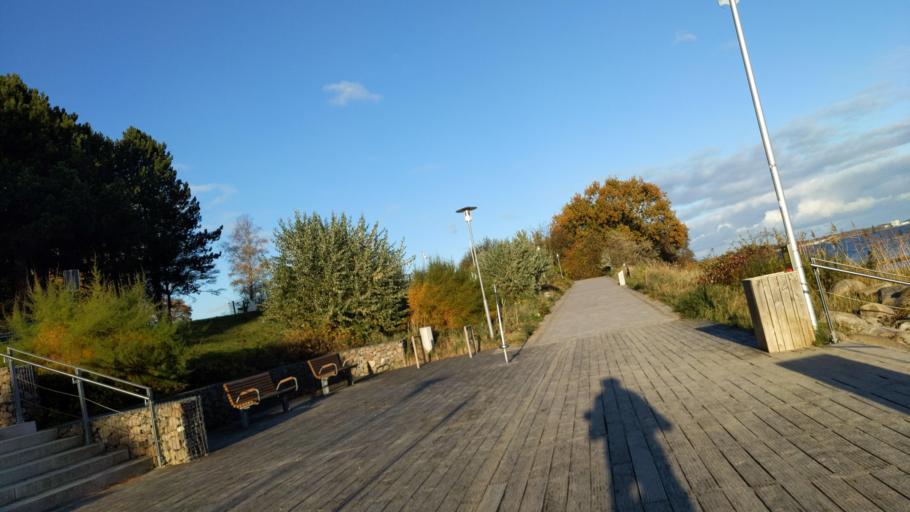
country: DE
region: Schleswig-Holstein
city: Sierksdorf
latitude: 54.0719
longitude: 10.7851
